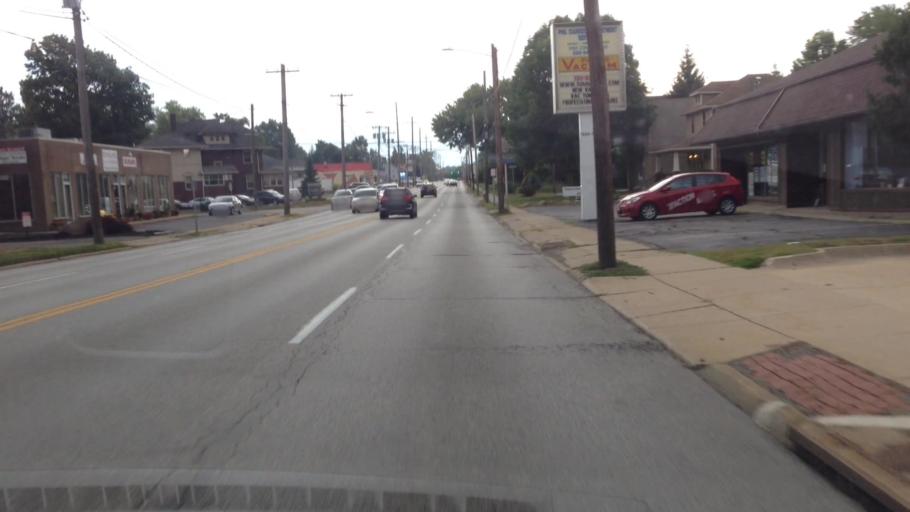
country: US
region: Ohio
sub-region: Summit County
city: Cuyahoga Falls
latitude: 41.1414
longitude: -81.4950
